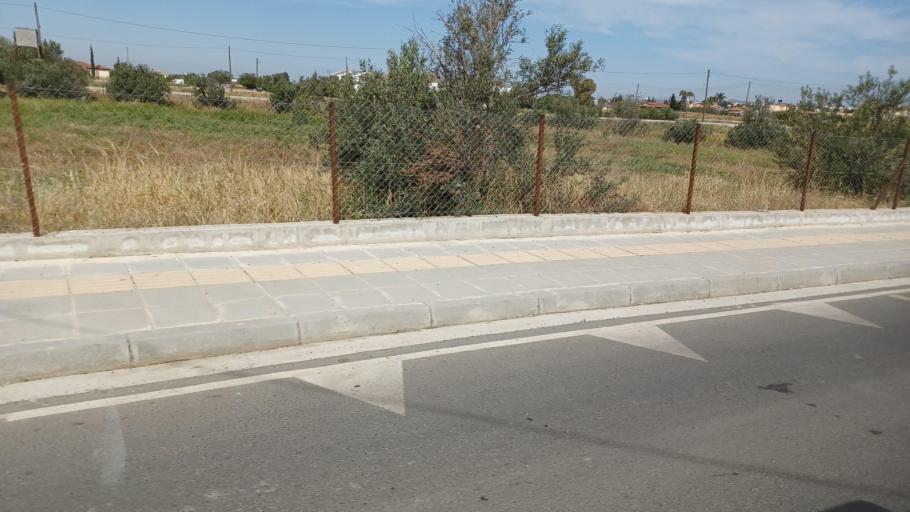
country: CY
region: Lefkosia
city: Kokkinotrimithia
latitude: 35.1561
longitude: 33.2054
